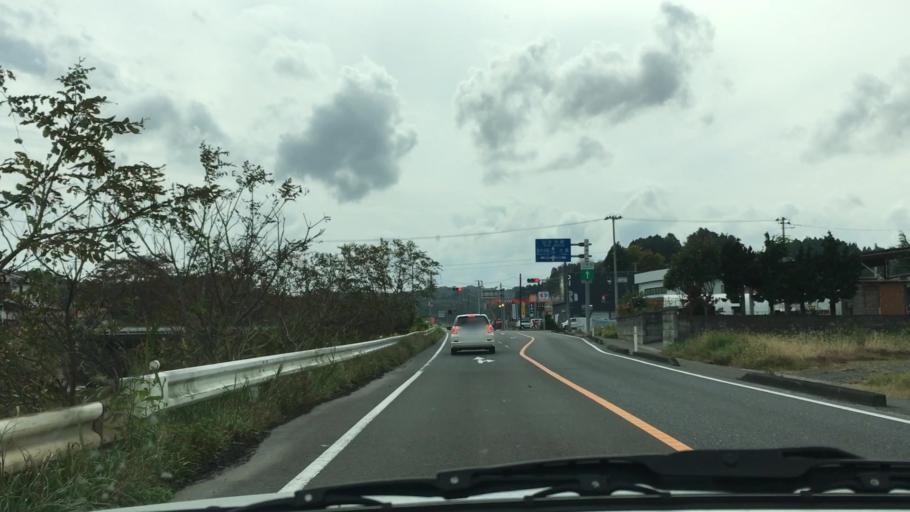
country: JP
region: Miyagi
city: Matsushima
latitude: 38.4370
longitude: 141.0652
